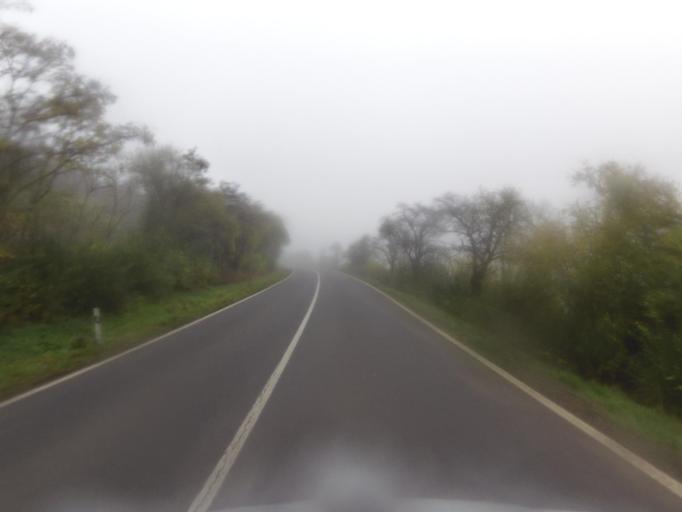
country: CZ
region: Ustecky
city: Libochovice
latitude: 50.3939
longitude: 13.9981
